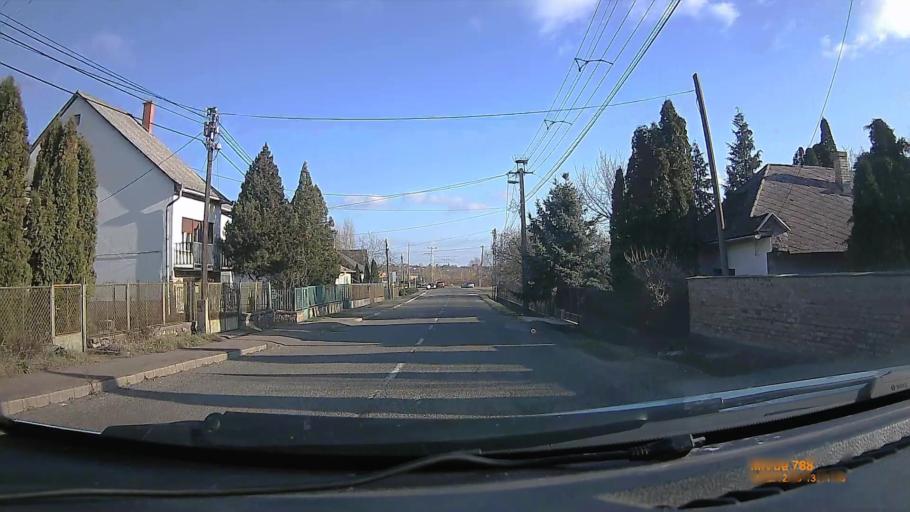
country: HU
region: Heves
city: Domoszlo
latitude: 47.8255
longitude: 20.0636
